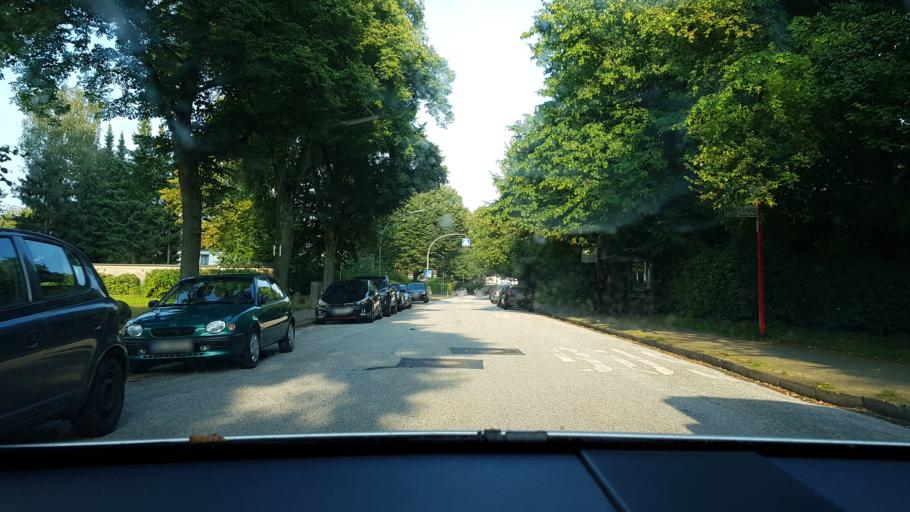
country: DE
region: Hamburg
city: Farmsen-Berne
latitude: 53.6276
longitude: 10.1118
